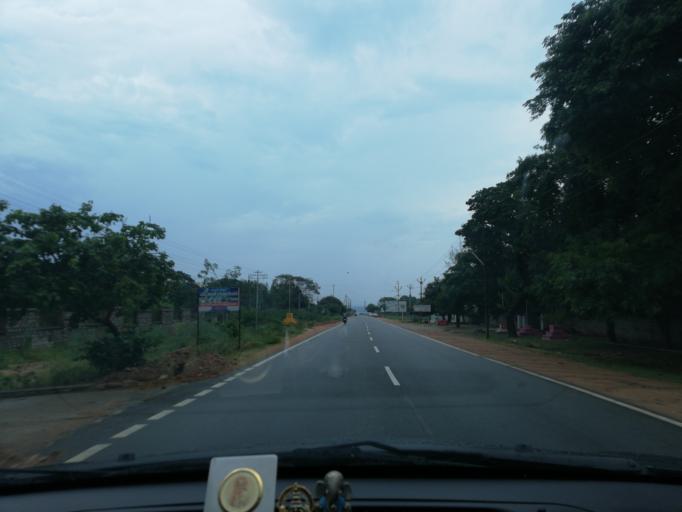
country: IN
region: Andhra Pradesh
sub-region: Guntur
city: Macherla
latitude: 16.6154
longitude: 79.2965
